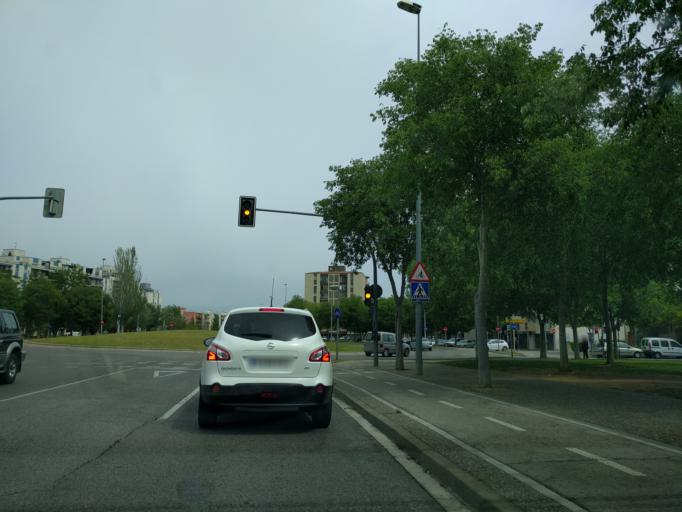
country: ES
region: Catalonia
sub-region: Provincia de Girona
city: Salt
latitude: 41.9706
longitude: 2.8087
